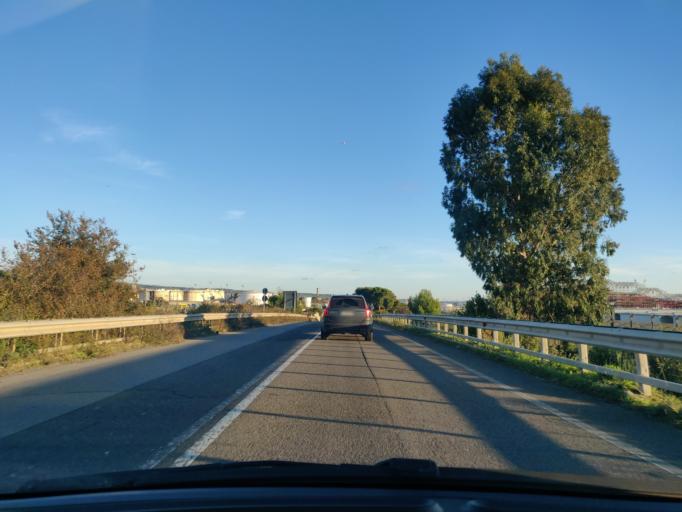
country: IT
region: Latium
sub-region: Citta metropolitana di Roma Capitale
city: Aurelia
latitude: 42.1148
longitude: 11.7730
